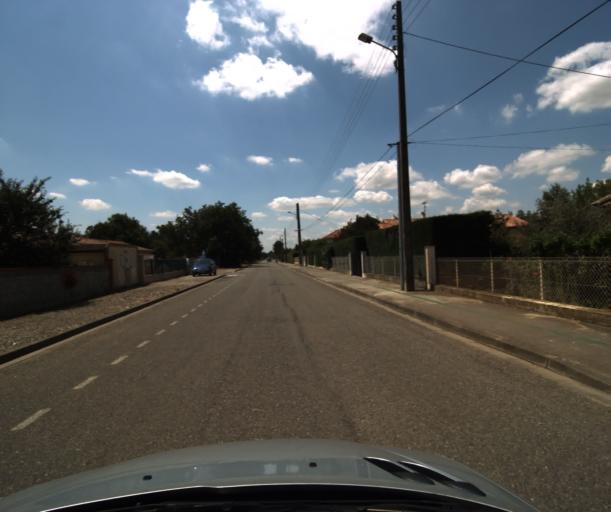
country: FR
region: Midi-Pyrenees
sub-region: Departement de la Haute-Garonne
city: Saint-Lys
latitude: 43.5093
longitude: 1.1784
